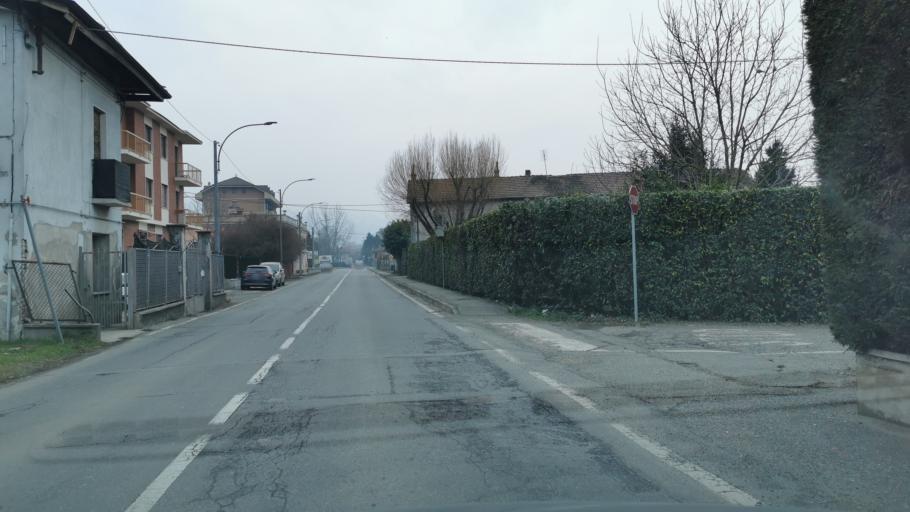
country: IT
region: Piedmont
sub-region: Provincia di Torino
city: San Mauro Torinese
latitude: 45.1120
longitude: 7.7586
